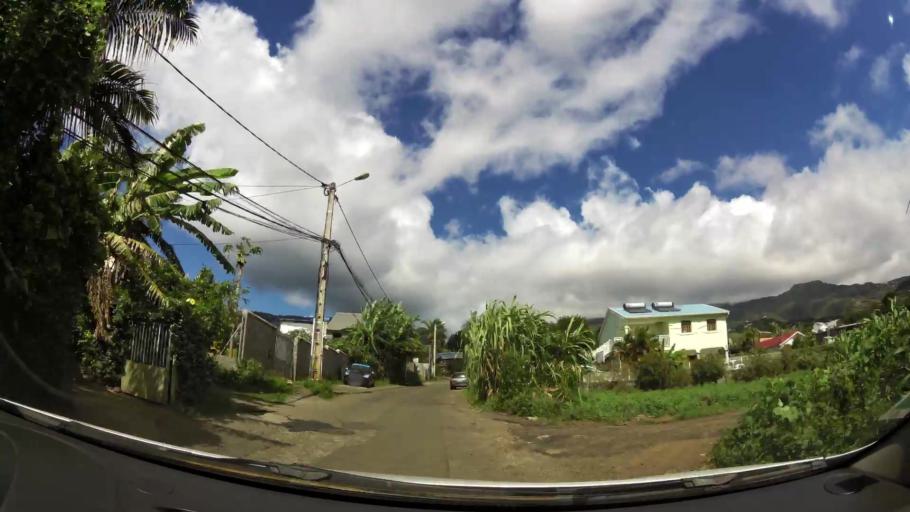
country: RE
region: Reunion
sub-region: Reunion
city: Sainte-Marie
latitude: -20.9229
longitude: 55.4994
